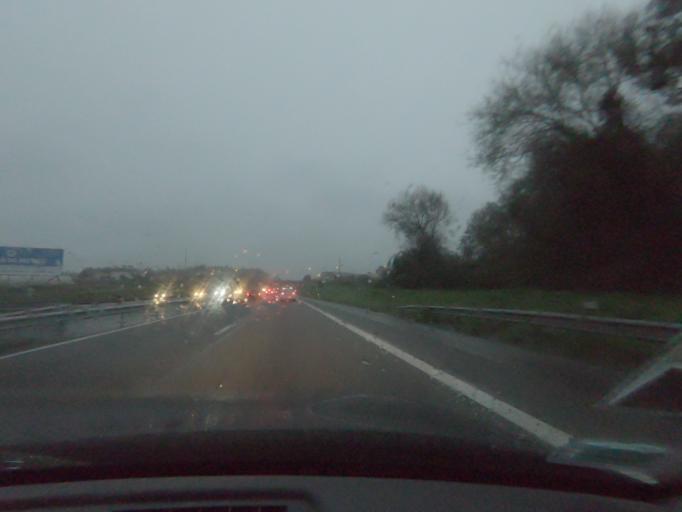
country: PT
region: Porto
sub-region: Matosinhos
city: Lavra
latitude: 41.2524
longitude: -8.6992
